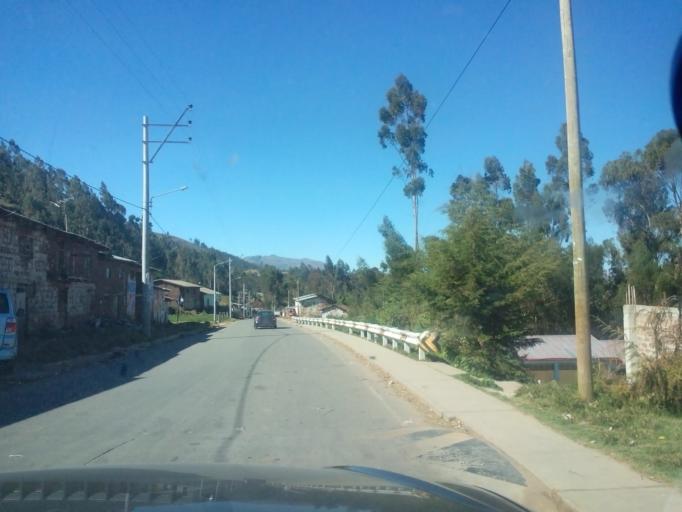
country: PE
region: Apurimac
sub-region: Provincia de Andahuaylas
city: Talavera
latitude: -13.6511
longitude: -73.5210
